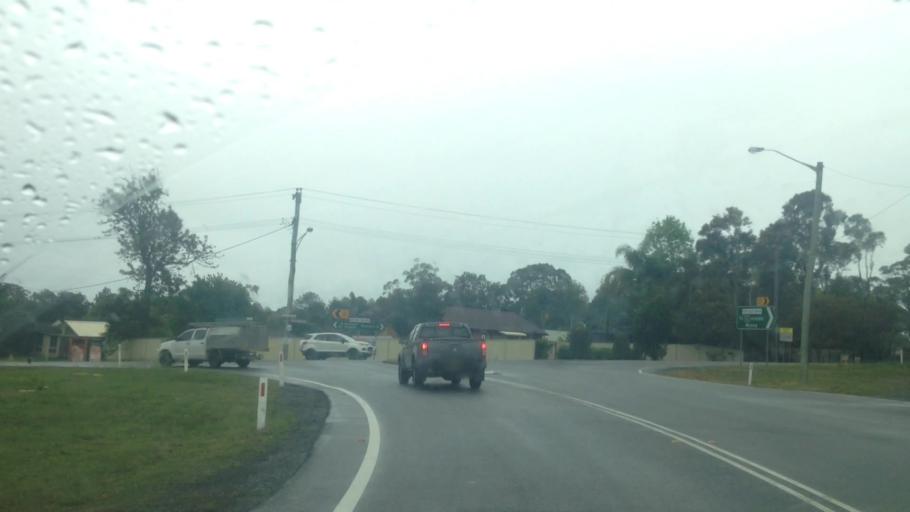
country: AU
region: New South Wales
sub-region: Wyong Shire
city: Charmhaven
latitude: -33.1762
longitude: 151.4808
